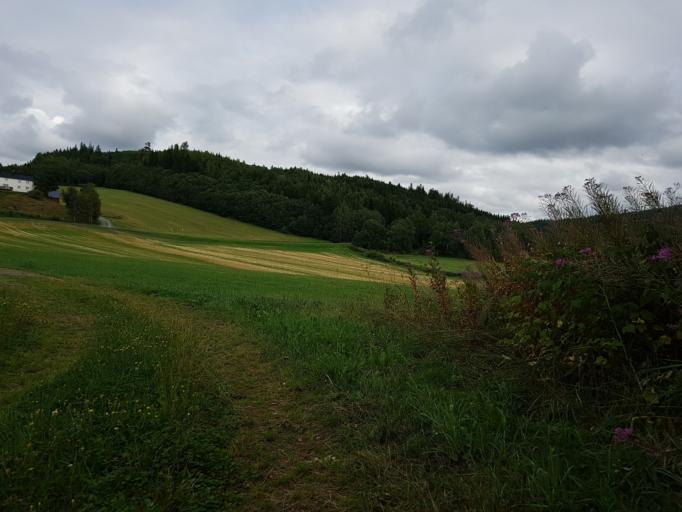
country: NO
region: Nord-Trondelag
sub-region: Levanger
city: Skogn
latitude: 63.6228
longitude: 11.2738
